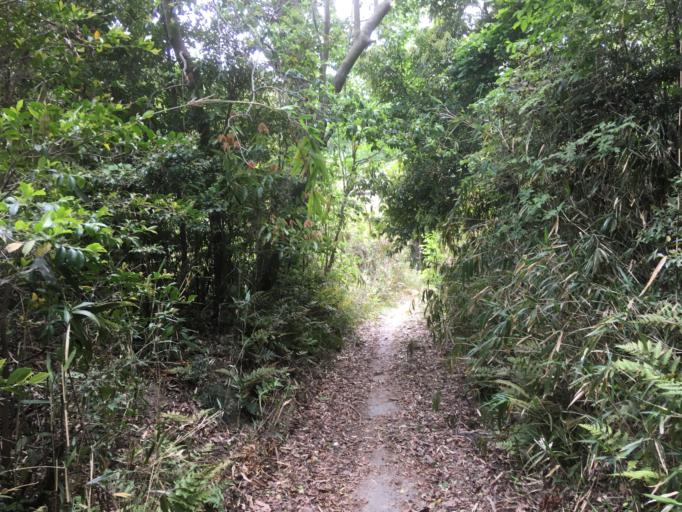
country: JP
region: Nara
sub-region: Ikoma-shi
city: Ikoma
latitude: 34.7039
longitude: 135.6747
